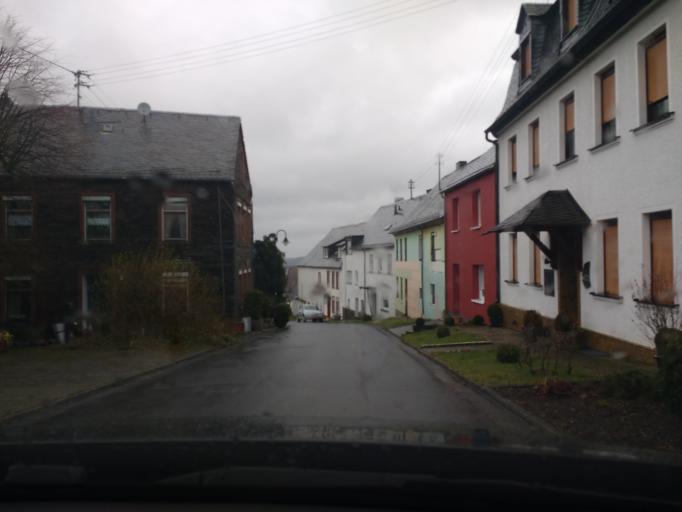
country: DE
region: Rheinland-Pfalz
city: Starkenburg
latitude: 49.9548
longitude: 7.1420
